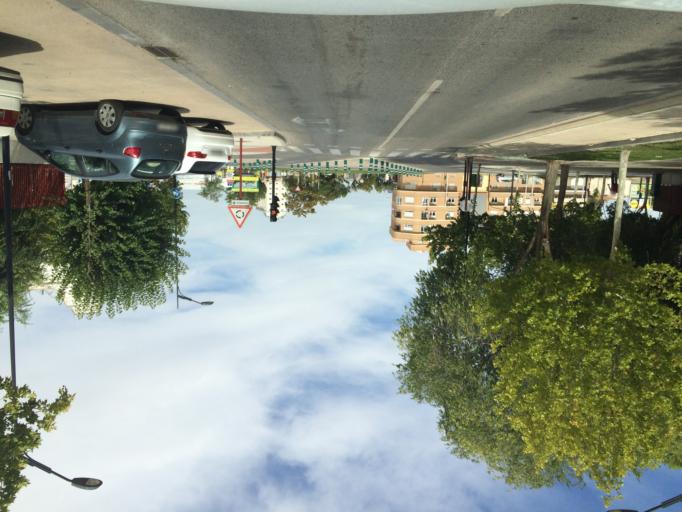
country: ES
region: Castille-La Mancha
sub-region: Provincia de Albacete
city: Albacete
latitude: 39.0079
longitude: -1.8633
